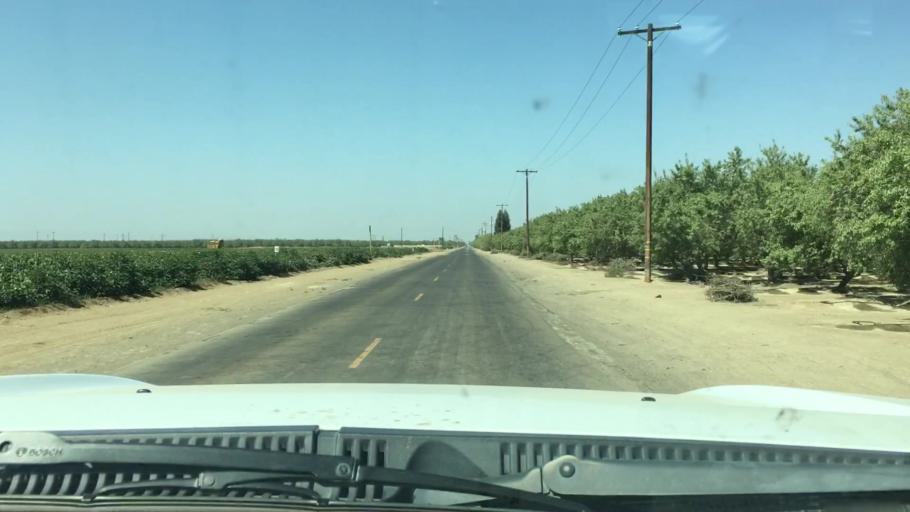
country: US
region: California
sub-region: Kern County
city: Shafter
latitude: 35.4794
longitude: -119.3140
